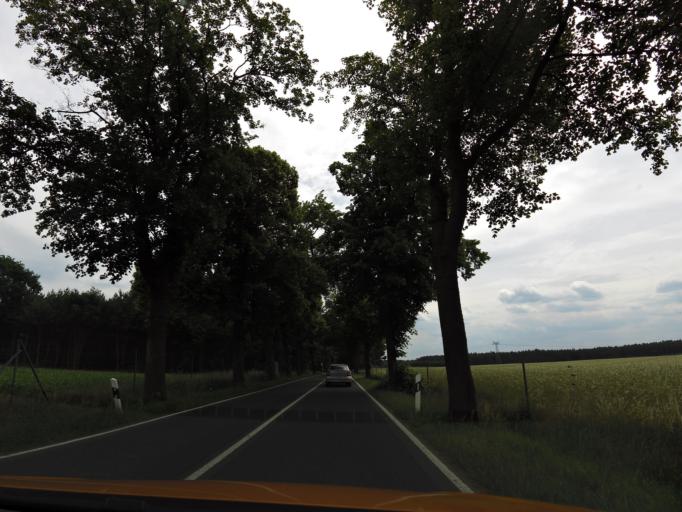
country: DE
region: Brandenburg
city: Am Mellensee
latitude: 52.2370
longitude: 13.3925
